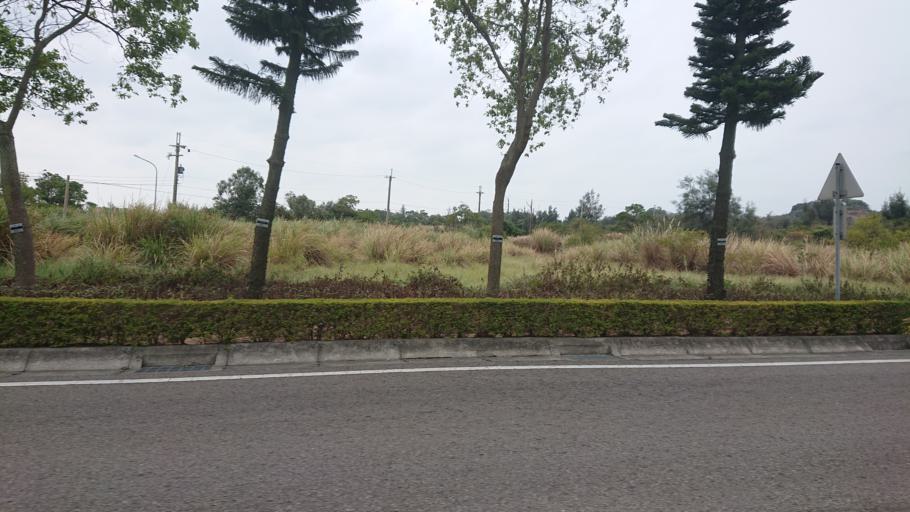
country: TW
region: Fukien
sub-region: Kinmen
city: Jincheng
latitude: 24.4123
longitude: 118.2934
